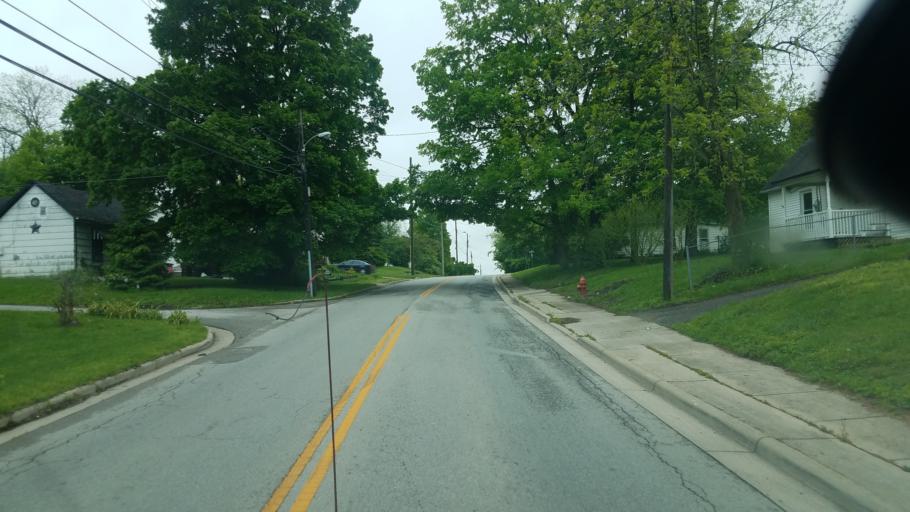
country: US
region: Ohio
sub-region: Highland County
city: Hillsboro
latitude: 39.2110
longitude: -83.6120
